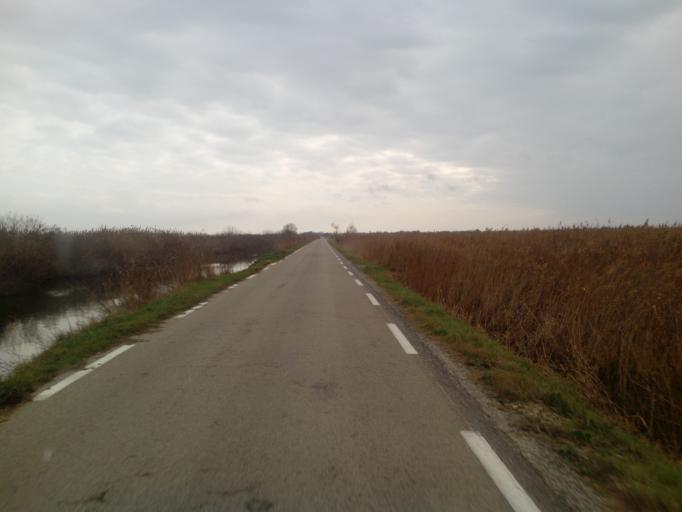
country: FR
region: Languedoc-Roussillon
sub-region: Departement du Gard
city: Vauvert
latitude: 43.6176
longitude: 4.3224
